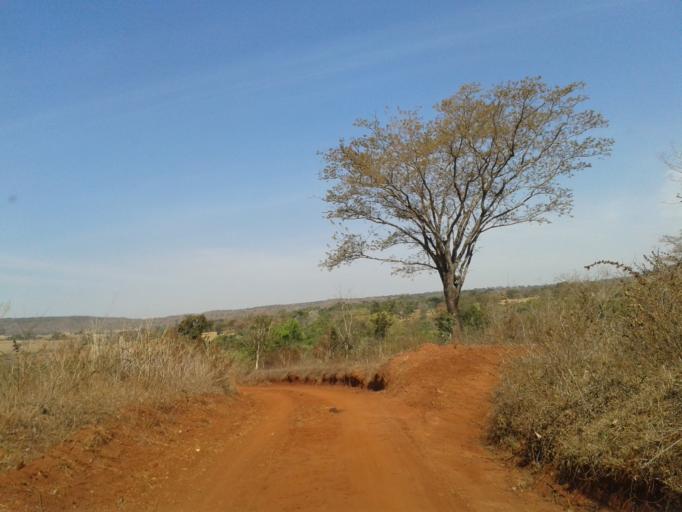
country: BR
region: Minas Gerais
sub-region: Santa Vitoria
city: Santa Vitoria
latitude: -19.2384
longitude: -50.0425
